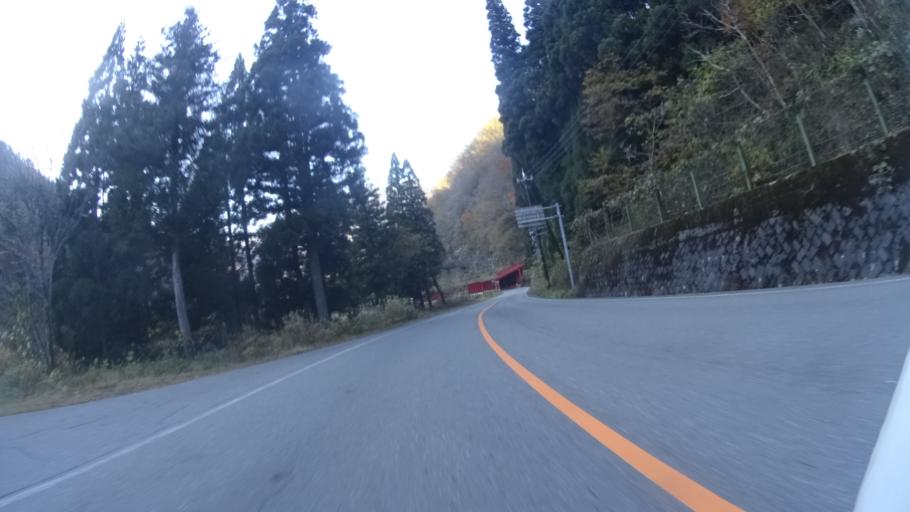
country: JP
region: Fukui
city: Ono
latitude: 35.9078
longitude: 136.6347
